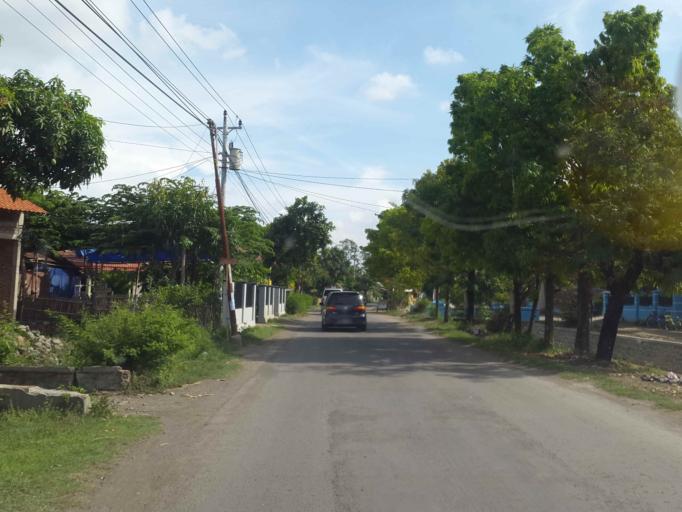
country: ID
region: Central Java
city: Pemalang
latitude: -6.9118
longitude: 109.3287
